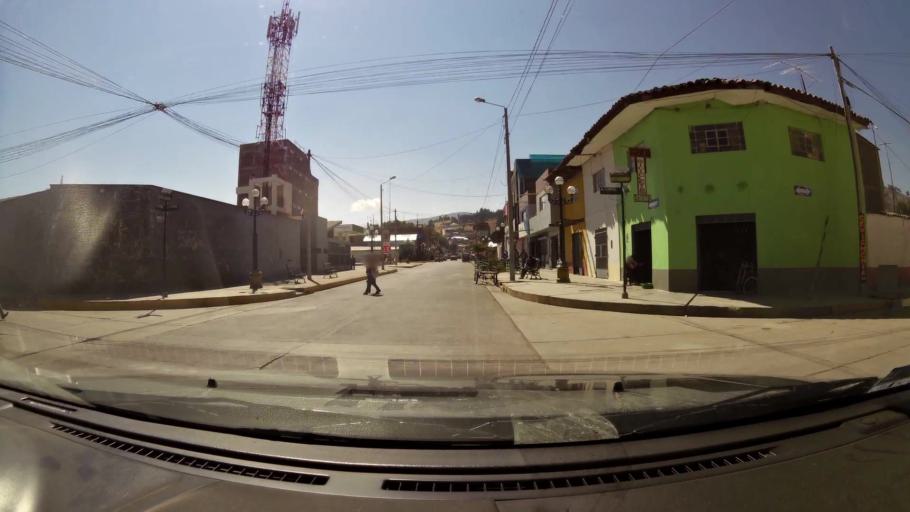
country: PE
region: Junin
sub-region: Provincia de Concepcion
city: Concepcion
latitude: -11.9197
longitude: -75.3146
